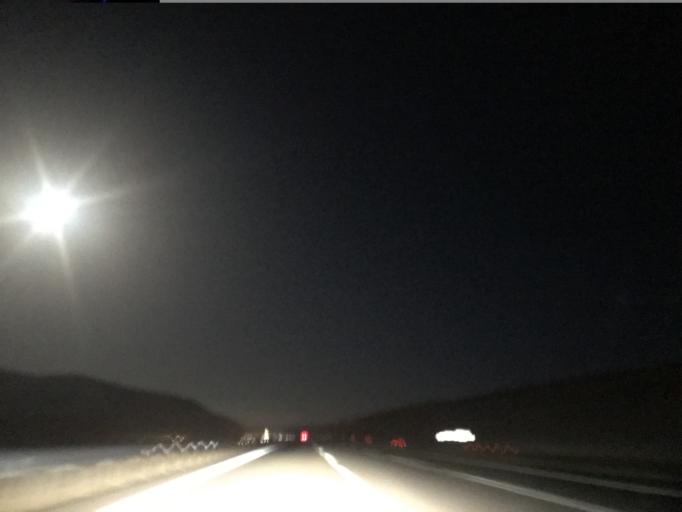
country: TR
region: Nigde
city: Ulukisla
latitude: 37.6429
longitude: 34.3767
